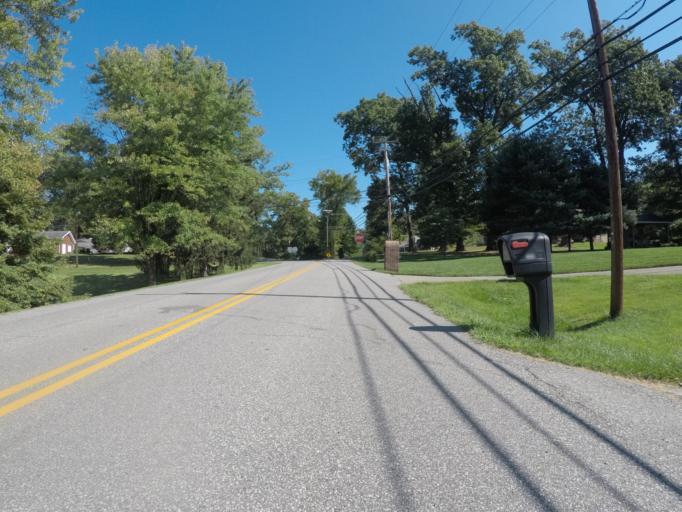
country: US
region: Kentucky
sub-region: Greenup County
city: Russell
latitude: 38.5193
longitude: -82.6953
